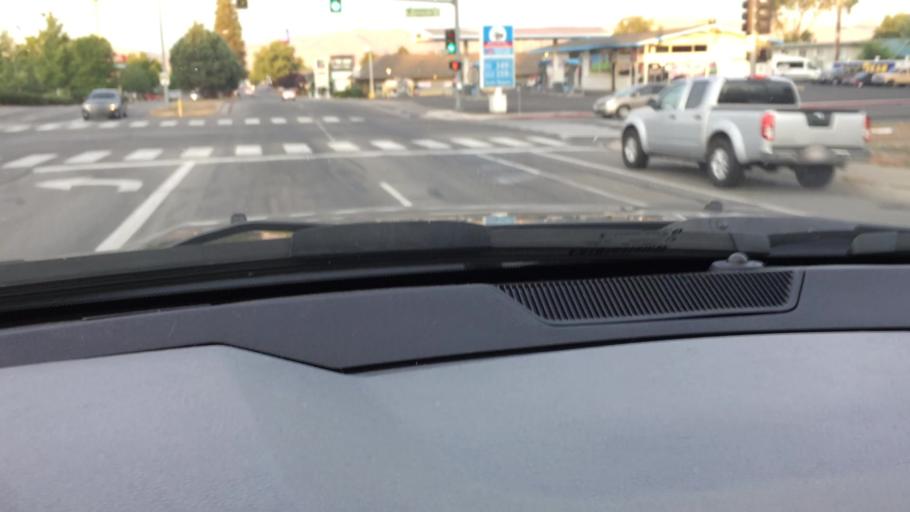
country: US
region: Nevada
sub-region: Washoe County
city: Reno
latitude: 39.5056
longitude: -119.8076
